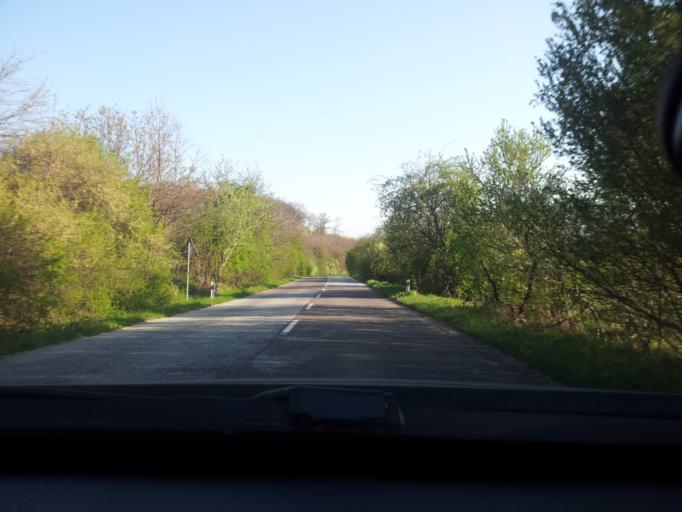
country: SK
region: Nitriansky
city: Tlmace
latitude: 48.2925
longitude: 18.4503
